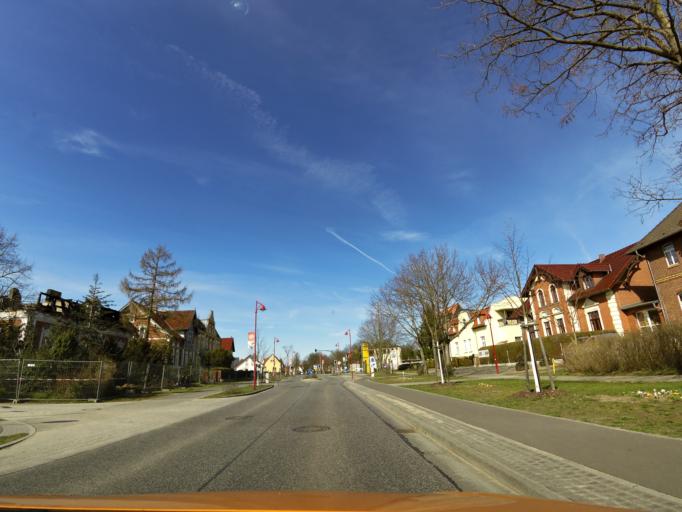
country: DE
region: Brandenburg
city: Beelitz
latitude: 52.2374
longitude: 12.9681
